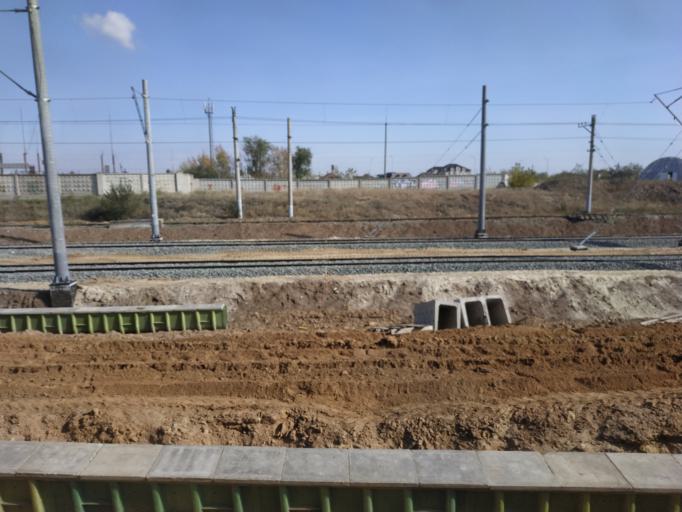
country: RU
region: Volgograd
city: Gumrak
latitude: 48.7737
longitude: 44.3835
